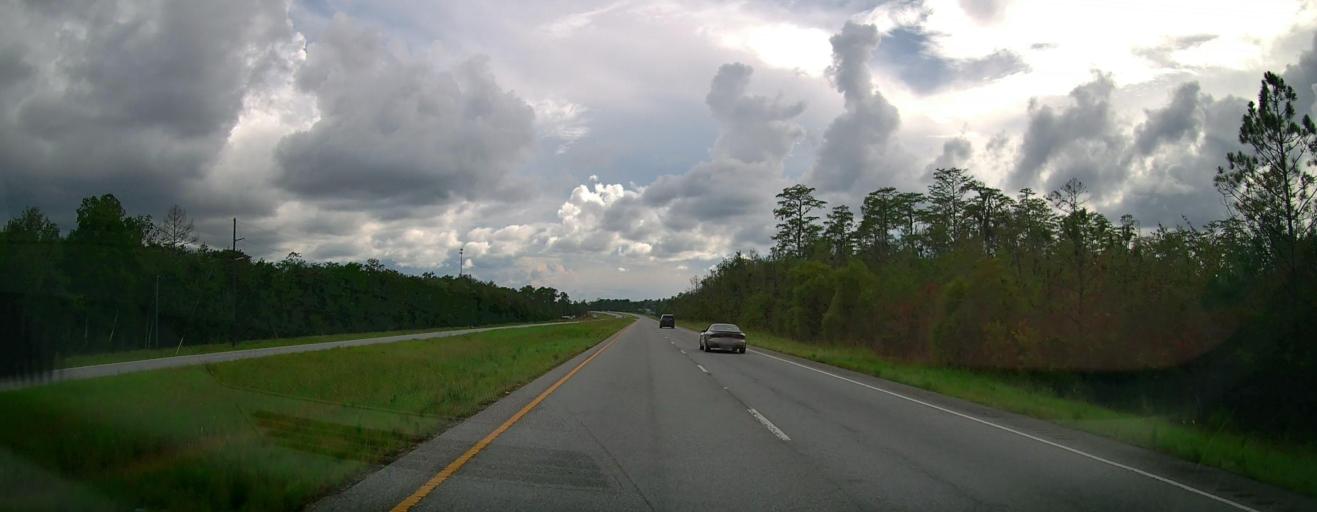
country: US
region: Georgia
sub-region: Pierce County
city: Blackshear
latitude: 31.4387
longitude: -82.0810
